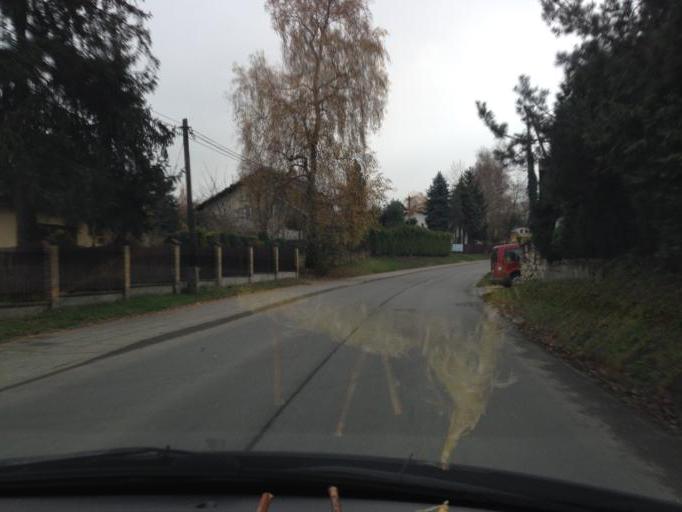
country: PL
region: Lesser Poland Voivodeship
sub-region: Powiat krakowski
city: Wrzasowice
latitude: 50.0042
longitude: 19.9485
